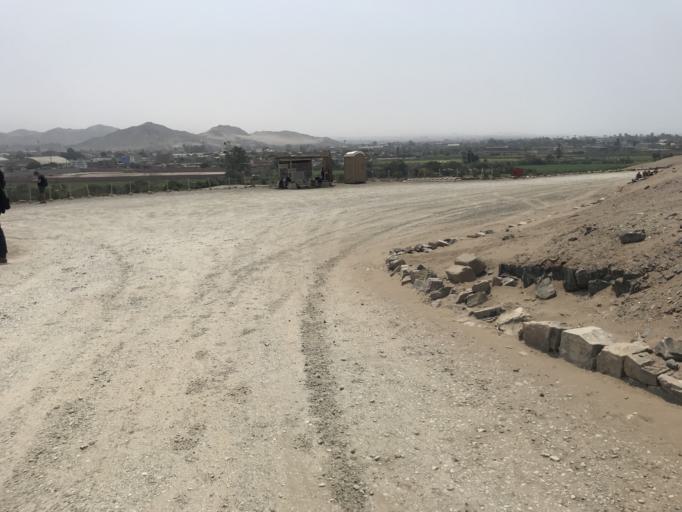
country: PE
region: Lima
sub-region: Lima
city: Punta Hermosa
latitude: -12.2553
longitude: -76.8965
